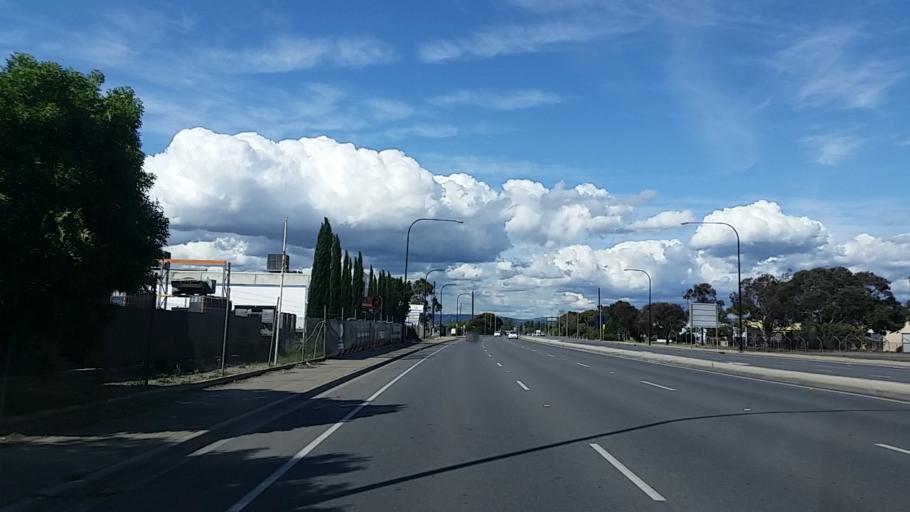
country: AU
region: South Australia
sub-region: Port Adelaide Enfield
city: Blair Athol
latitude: -34.8495
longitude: 138.5665
